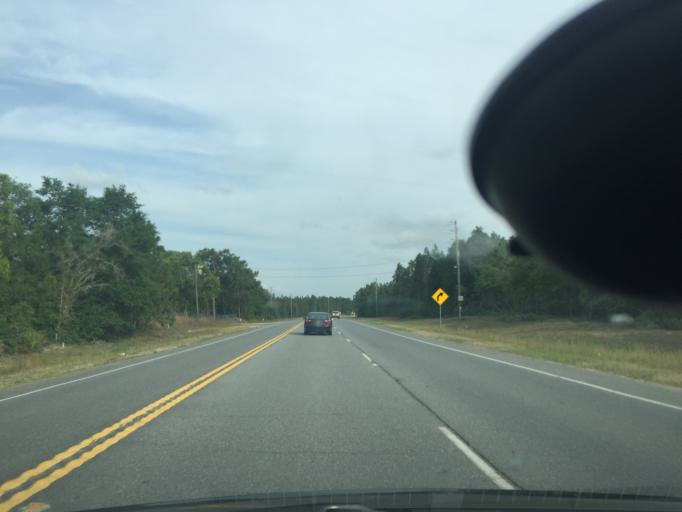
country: US
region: Georgia
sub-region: Chatham County
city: Bloomingdale
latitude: 32.0584
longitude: -81.3496
